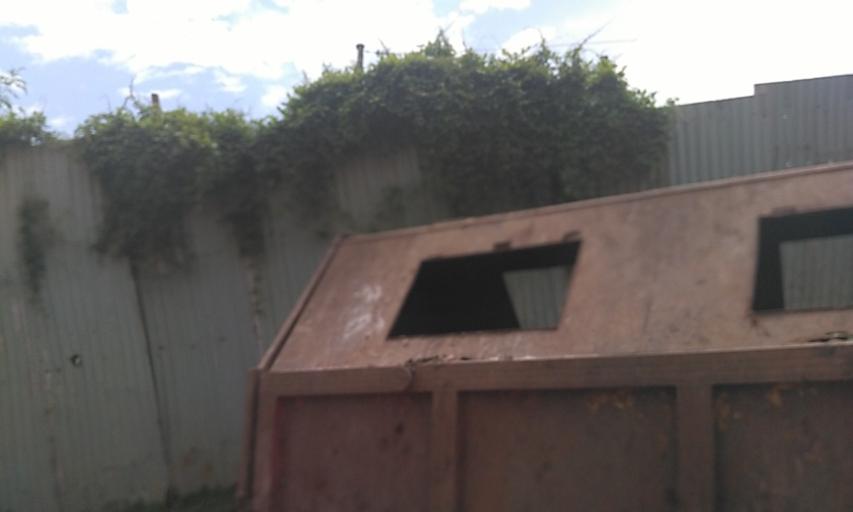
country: UG
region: Central Region
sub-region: Kampala District
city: Kampala
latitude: 0.3321
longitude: 32.6063
